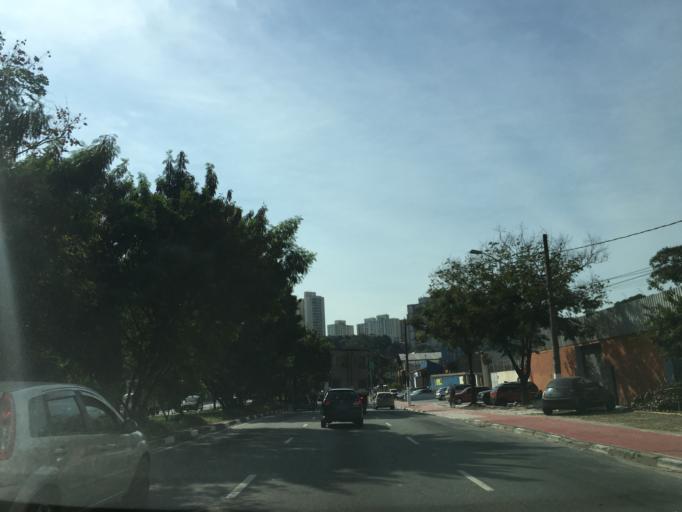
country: BR
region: Sao Paulo
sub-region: Osasco
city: Osasco
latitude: -23.5612
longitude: -46.7486
